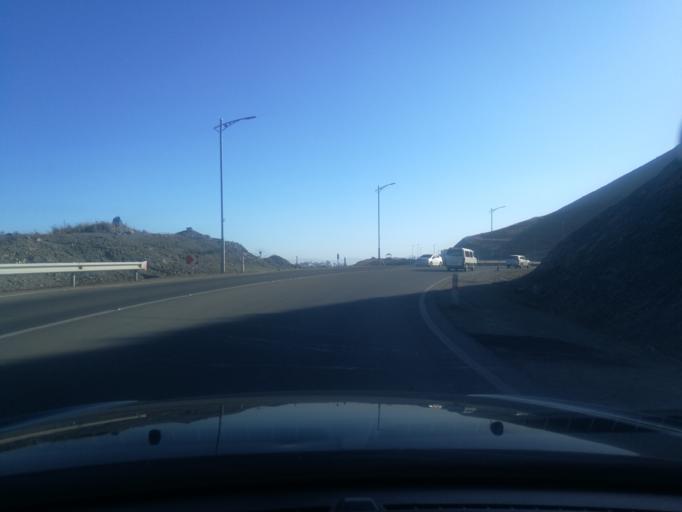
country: MN
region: Ulaanbaatar
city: Ulaanbaatar
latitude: 47.8863
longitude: 106.8683
